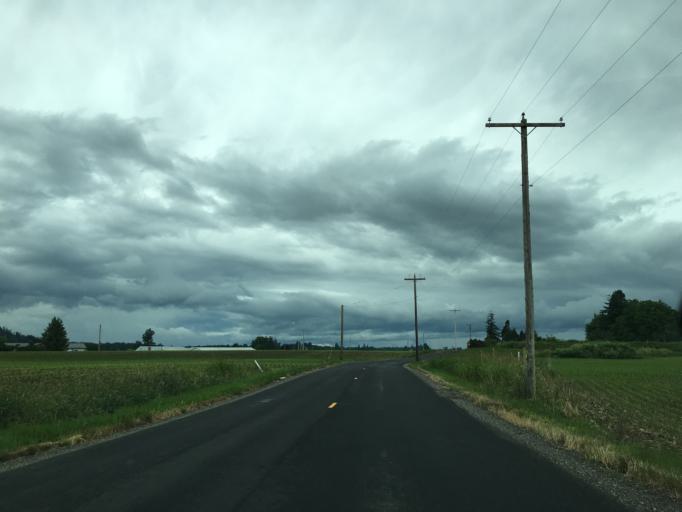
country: US
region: Washington
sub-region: Whatcom County
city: Sumas
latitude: 48.9766
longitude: -122.2554
